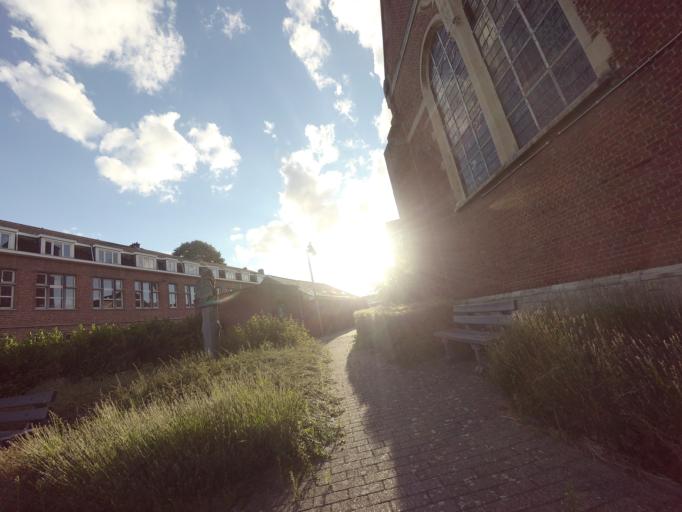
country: BE
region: Flanders
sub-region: Provincie Vlaams-Brabant
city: Kapelle-op-den-Bos
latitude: 51.0131
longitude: 4.3551
